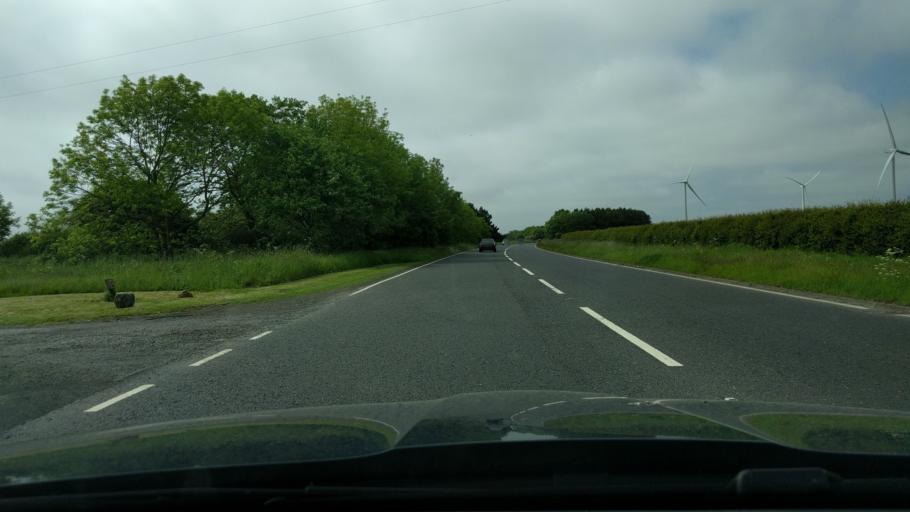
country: GB
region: England
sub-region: Northumberland
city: East Chevington
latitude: 55.2732
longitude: -1.6018
